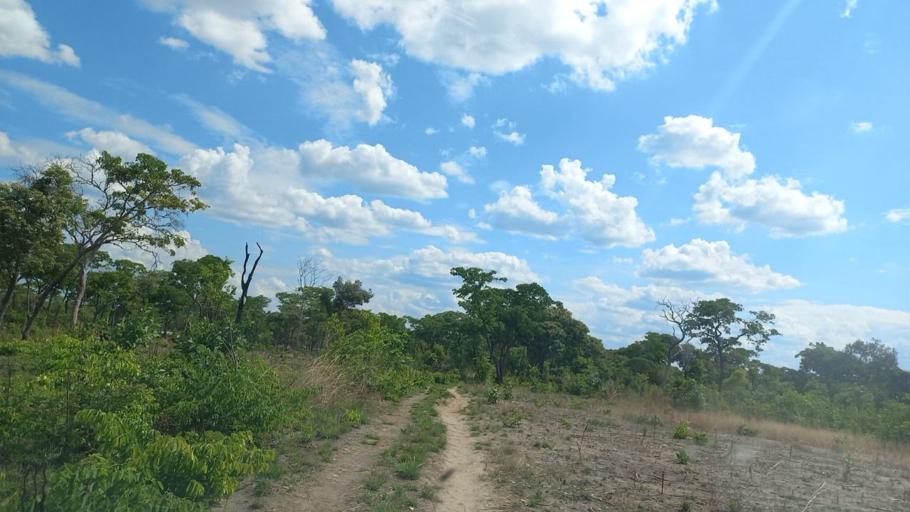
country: ZM
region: North-Western
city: Mufumbwe
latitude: -13.3435
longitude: 24.6309
